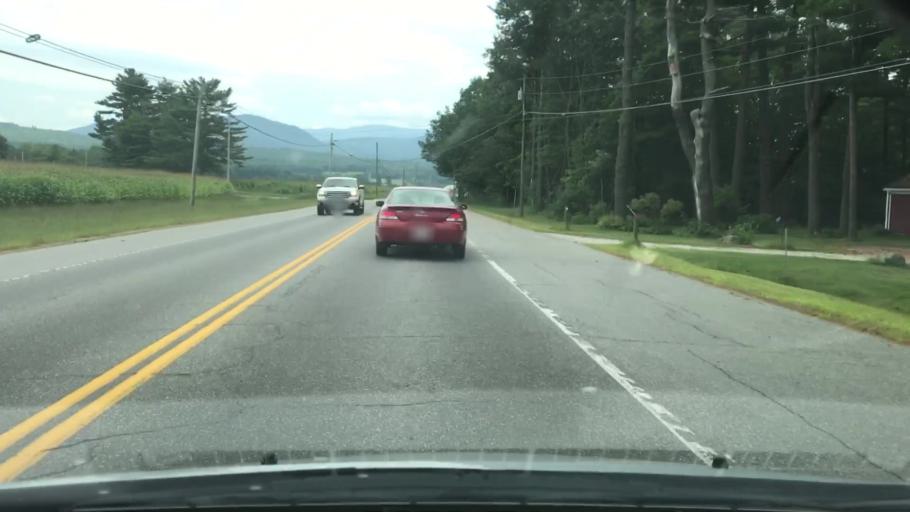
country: US
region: New Hampshire
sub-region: Grafton County
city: North Haverhill
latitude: 44.1055
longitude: -72.0343
